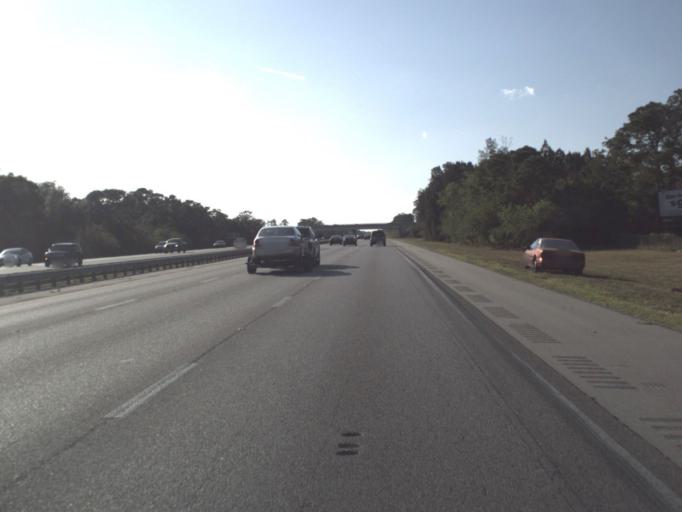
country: US
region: Florida
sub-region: Brevard County
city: West Melbourne
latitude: 28.0459
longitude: -80.6663
